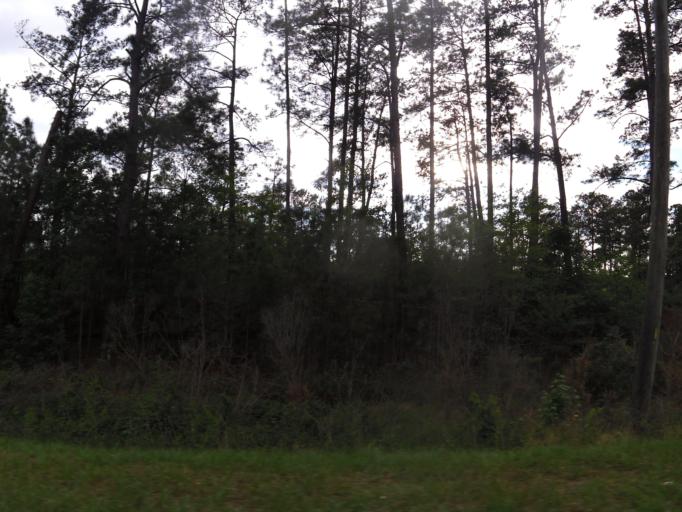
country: US
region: South Carolina
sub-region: Jasper County
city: Hardeeville
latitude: 32.3887
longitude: -81.0979
